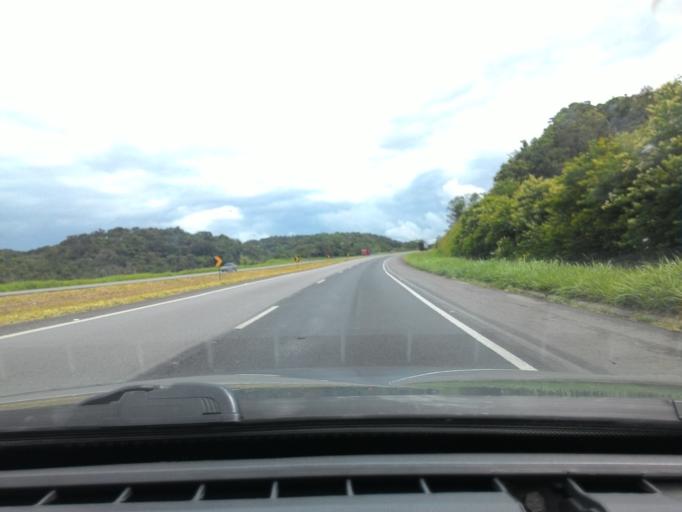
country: BR
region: Sao Paulo
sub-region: Registro
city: Registro
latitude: -24.5838
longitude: -47.8840
